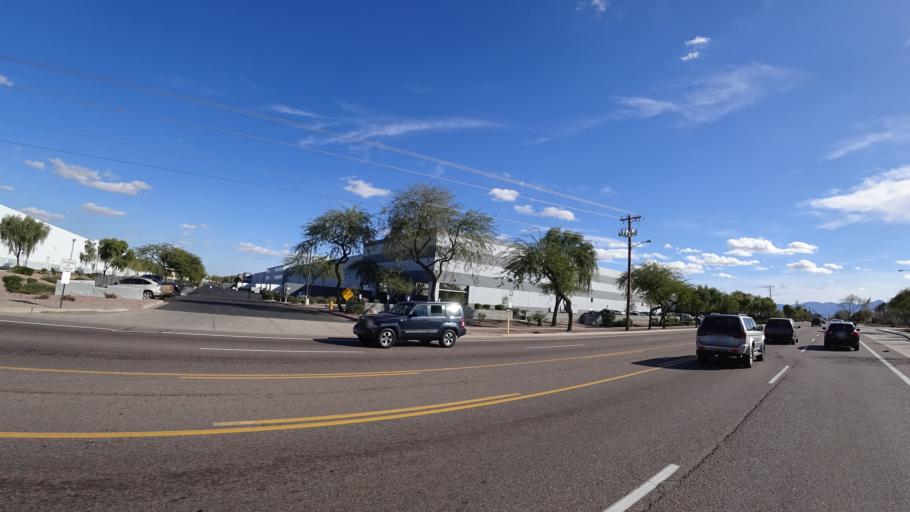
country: US
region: Arizona
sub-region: Maricopa County
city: Tolleson
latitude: 33.4570
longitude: -112.2210
